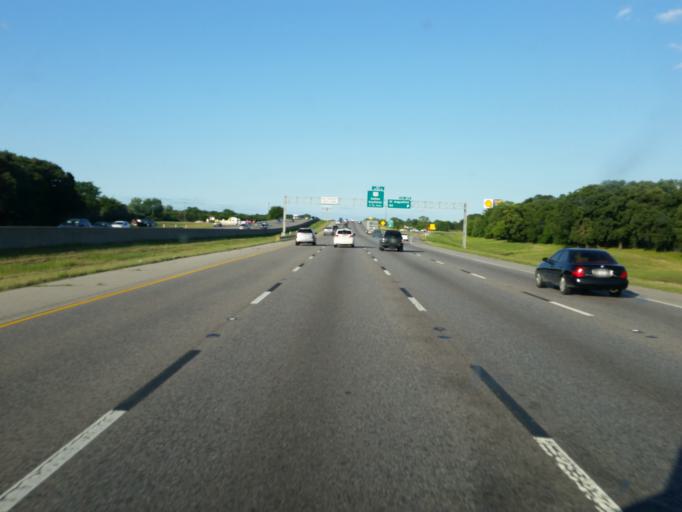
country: US
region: Texas
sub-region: Dallas County
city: Hutchins
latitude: 32.6816
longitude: -96.6627
